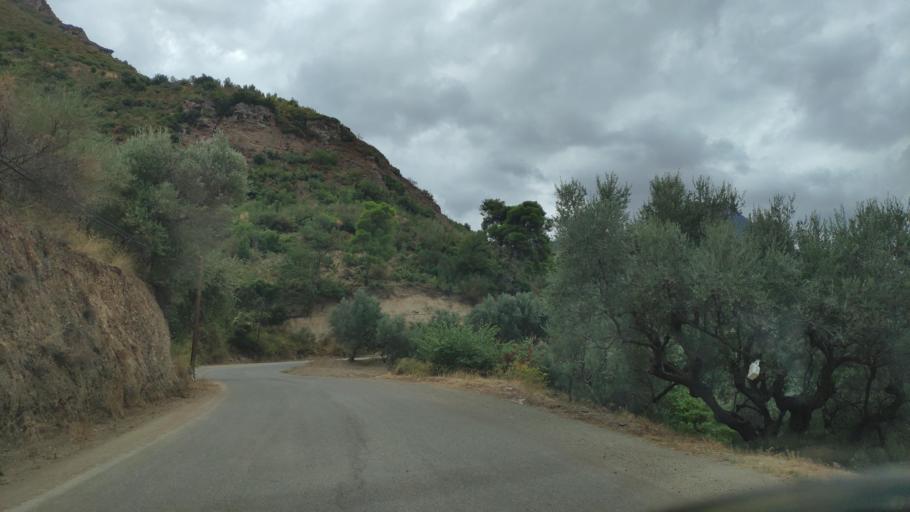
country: GR
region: West Greece
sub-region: Nomos Achaias
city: Temeni
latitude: 38.1840
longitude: 22.1480
